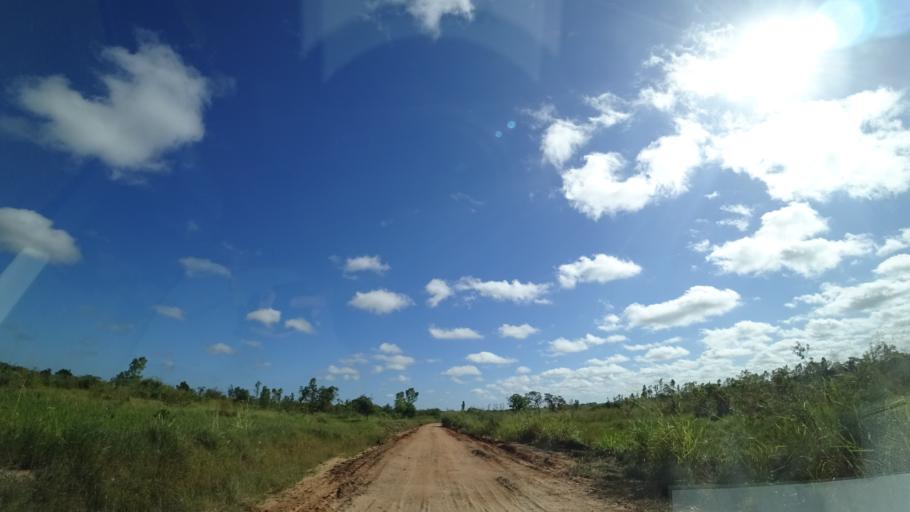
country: MZ
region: Sofala
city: Dondo
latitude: -19.4273
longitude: 34.7079
